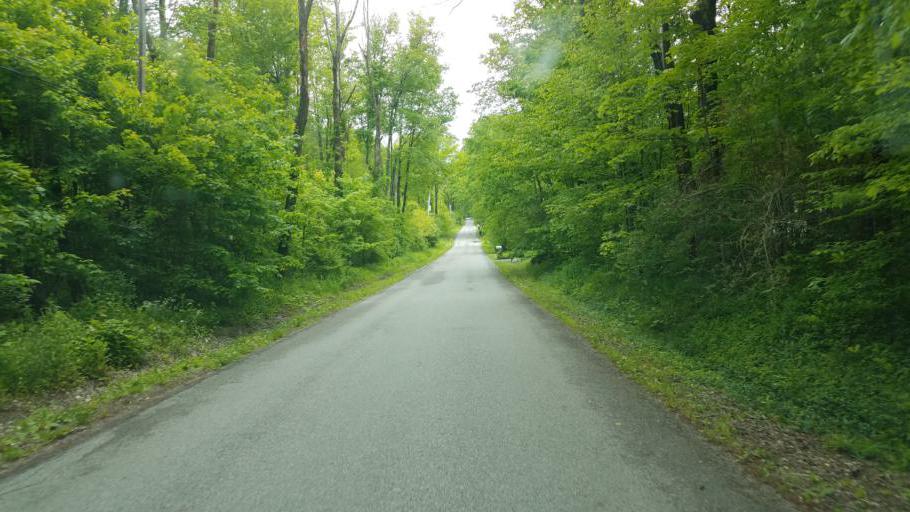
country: US
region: Ohio
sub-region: Geauga County
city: Burton
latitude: 41.4228
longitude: -81.1906
